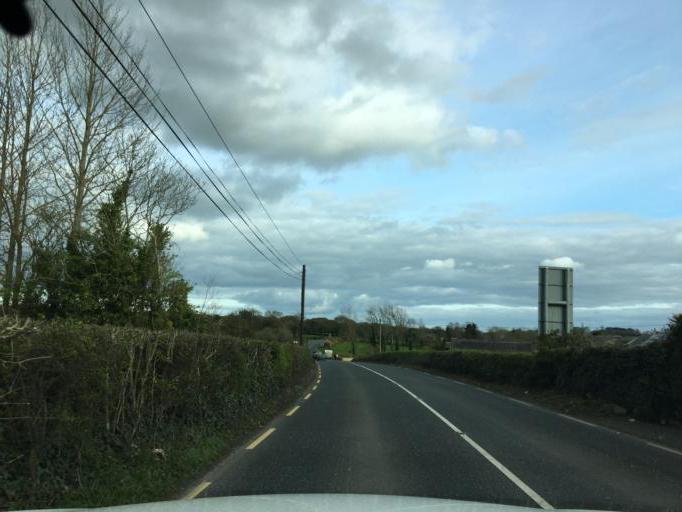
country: IE
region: Leinster
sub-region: Loch Garman
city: New Ross
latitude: 52.4346
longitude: -6.9589
